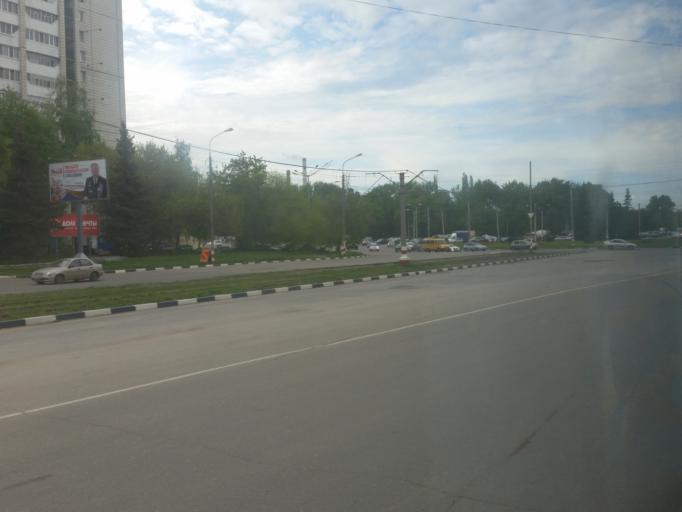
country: RU
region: Ulyanovsk
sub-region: Ulyanovskiy Rayon
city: Ulyanovsk
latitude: 54.3050
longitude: 48.3497
